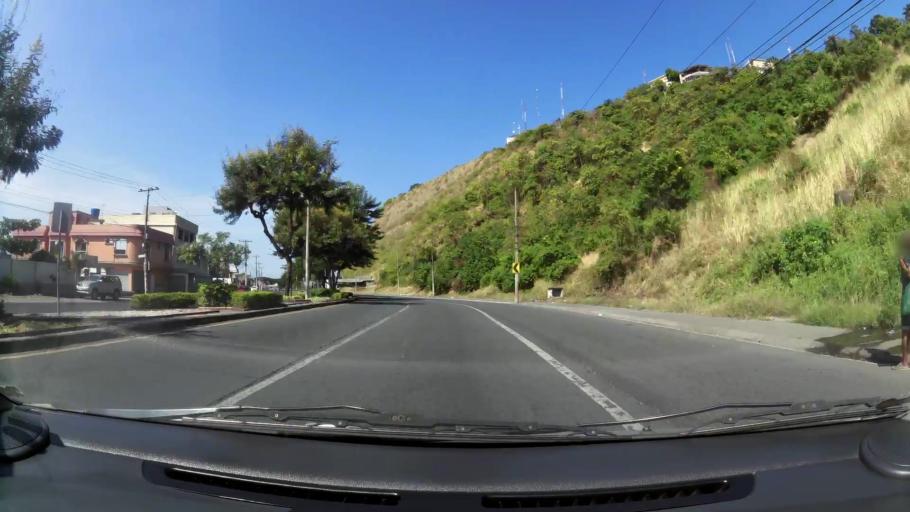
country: EC
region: Guayas
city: Guayaquil
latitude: -2.1820
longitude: -79.9124
